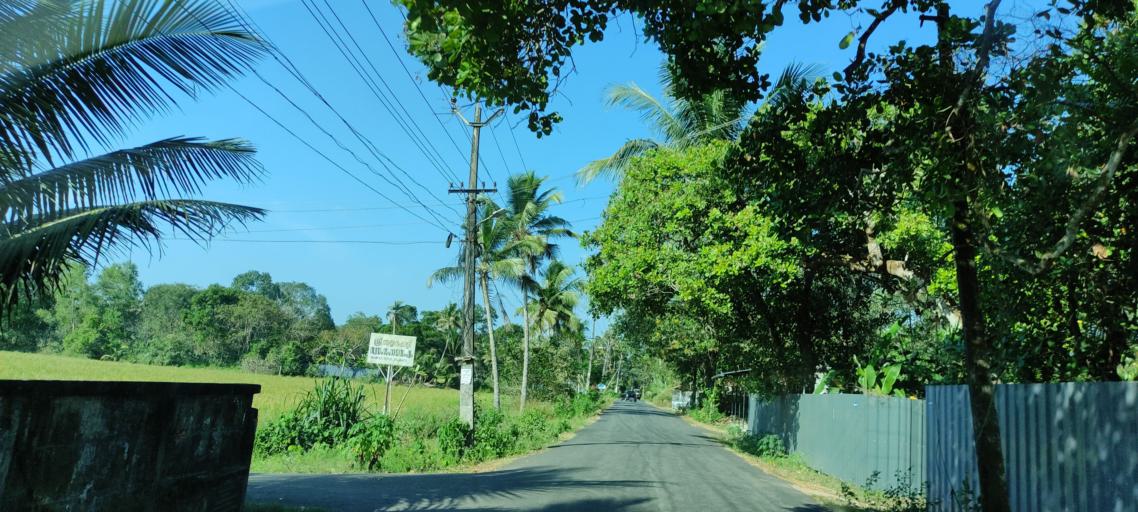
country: IN
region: Kerala
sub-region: Alappuzha
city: Shertallai
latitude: 9.6148
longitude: 76.3407
